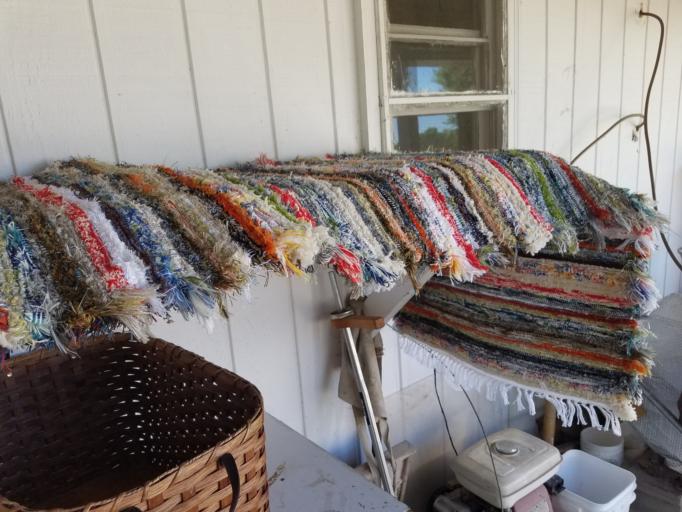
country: US
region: Missouri
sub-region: Carroll County
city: Carrollton
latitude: 39.4426
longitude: -93.4765
